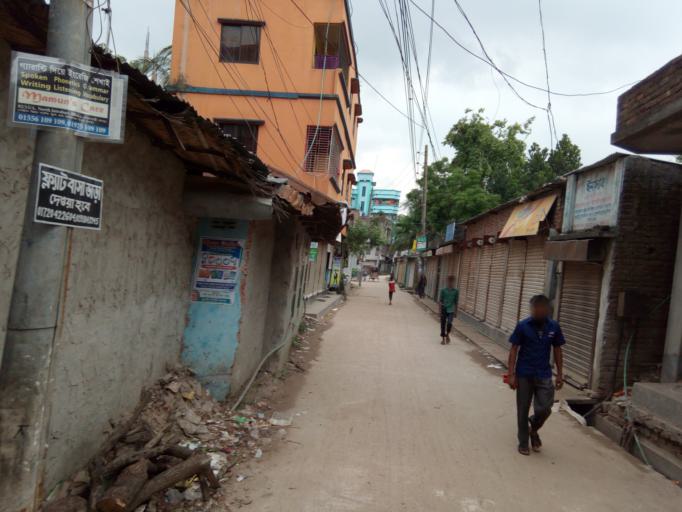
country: BD
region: Dhaka
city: Paltan
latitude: 23.7111
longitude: 90.4919
